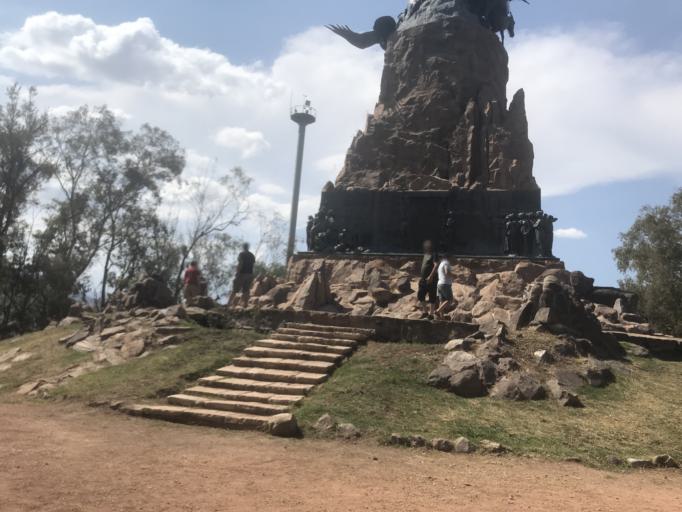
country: AR
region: Mendoza
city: Mendoza
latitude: -32.8890
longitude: -68.8912
